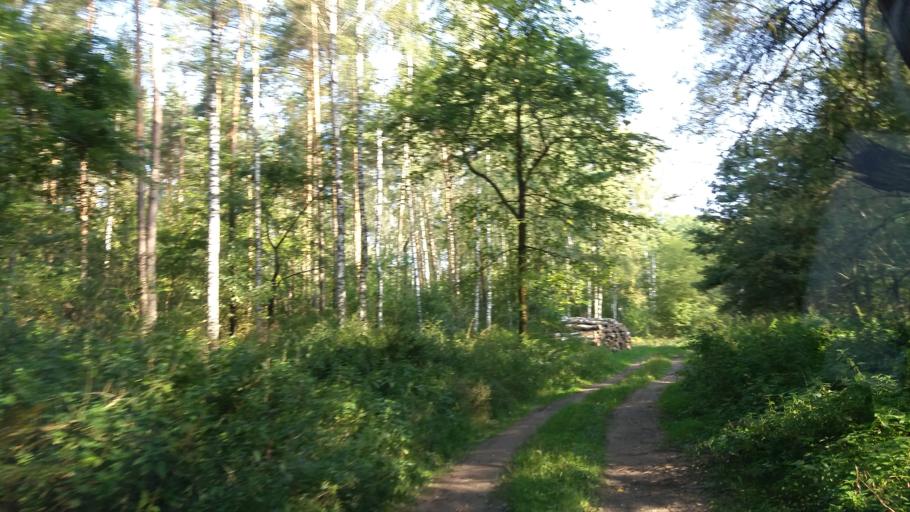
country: PL
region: West Pomeranian Voivodeship
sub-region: Powiat choszczenski
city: Recz
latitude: 53.1929
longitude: 15.5412
